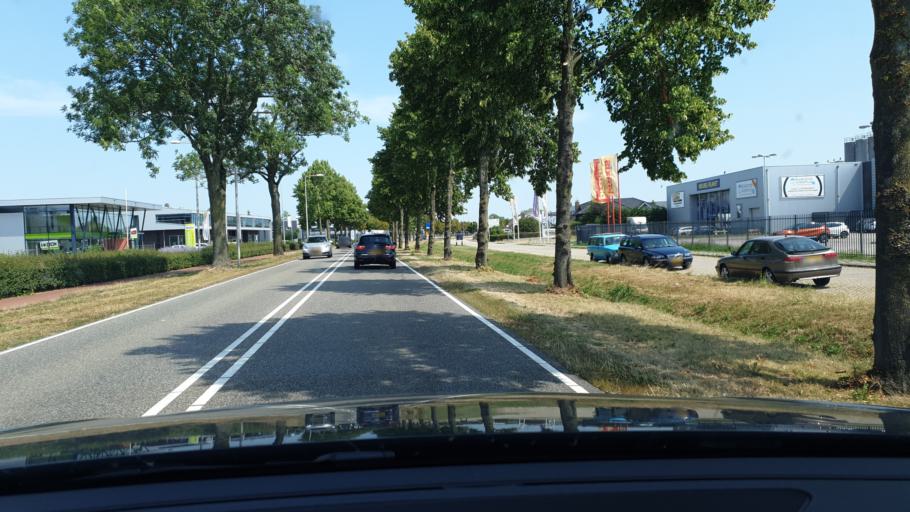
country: NL
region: Gelderland
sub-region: Gemeente Arnhem
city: Arnhem
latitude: 51.9122
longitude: 5.9171
